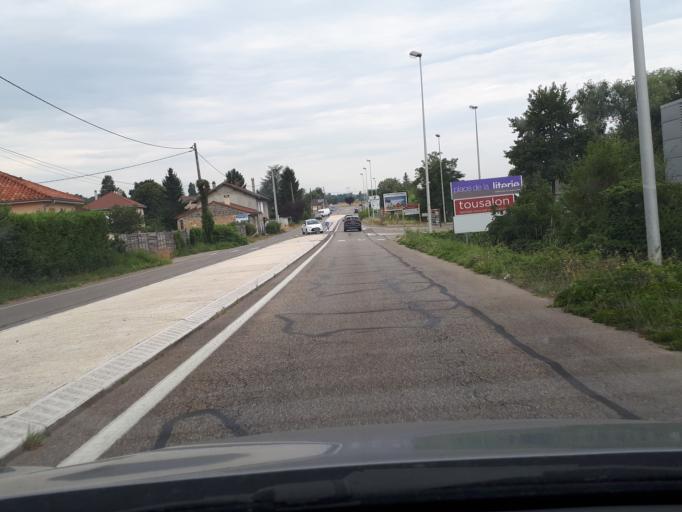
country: FR
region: Rhone-Alpes
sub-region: Departement de l'Isere
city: Domarin
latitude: 45.5870
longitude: 5.2533
